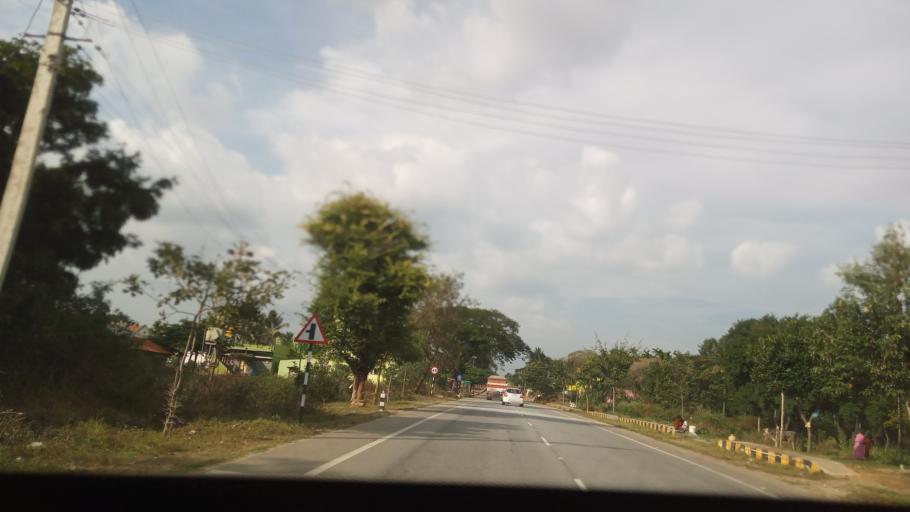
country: IN
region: Karnataka
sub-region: Tumkur
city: Kunigal
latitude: 12.8642
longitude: 77.0399
